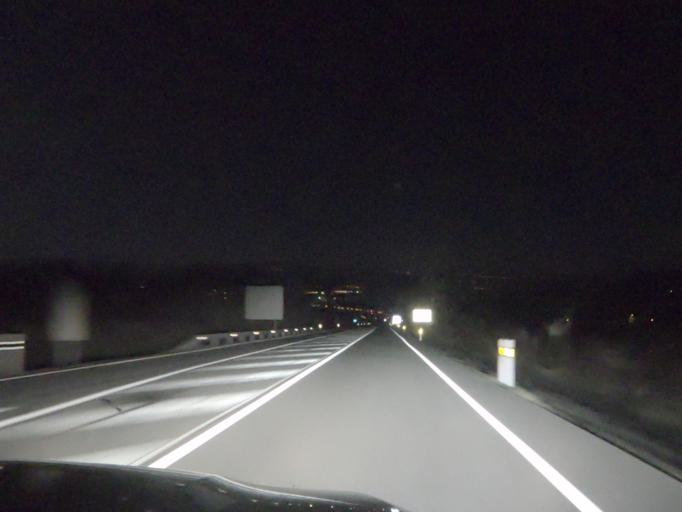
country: ES
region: Galicia
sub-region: Provincia de Ourense
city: Cualedro
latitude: 41.9800
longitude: -7.5249
